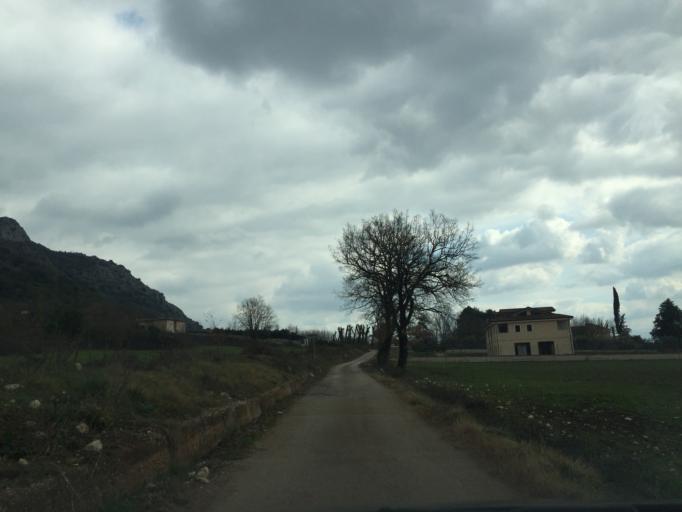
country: IT
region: Latium
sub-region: Provincia di Frosinone
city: Villa Santa Lucia
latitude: 41.4876
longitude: 13.7907
